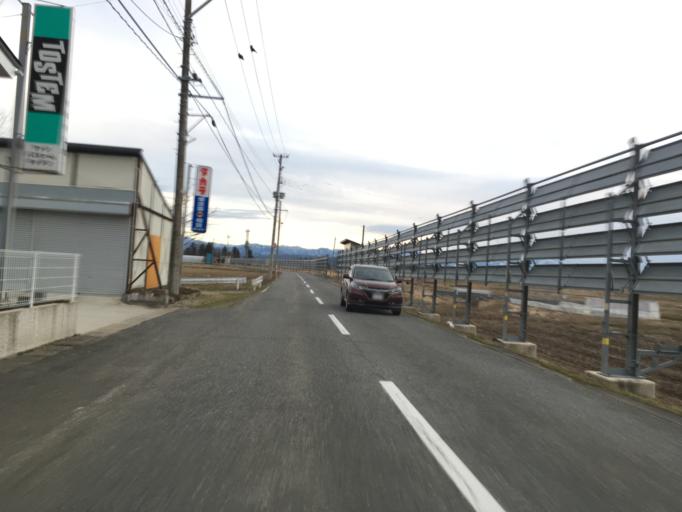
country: JP
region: Yamagata
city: Nagai
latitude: 38.0184
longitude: 140.0796
